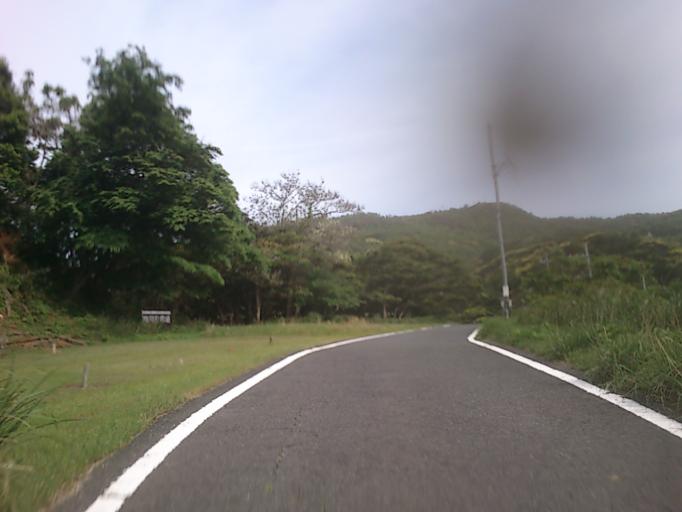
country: JP
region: Hyogo
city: Toyooka
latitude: 35.6900
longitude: 134.9908
